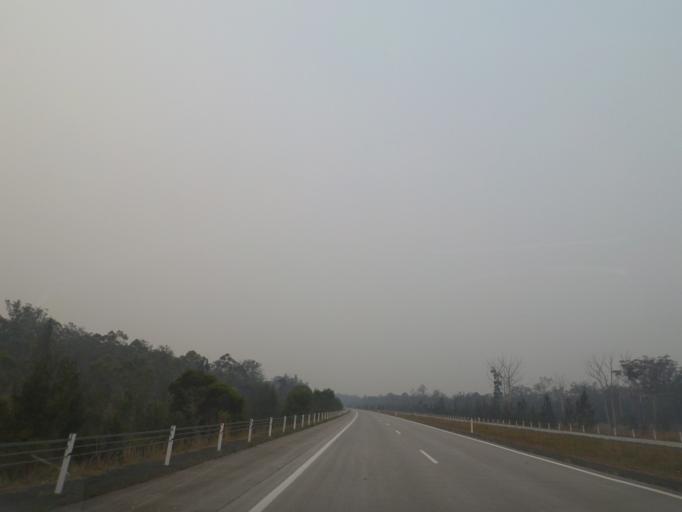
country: AU
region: New South Wales
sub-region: Kempsey
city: Frederickton
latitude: -31.0779
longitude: 152.8804
